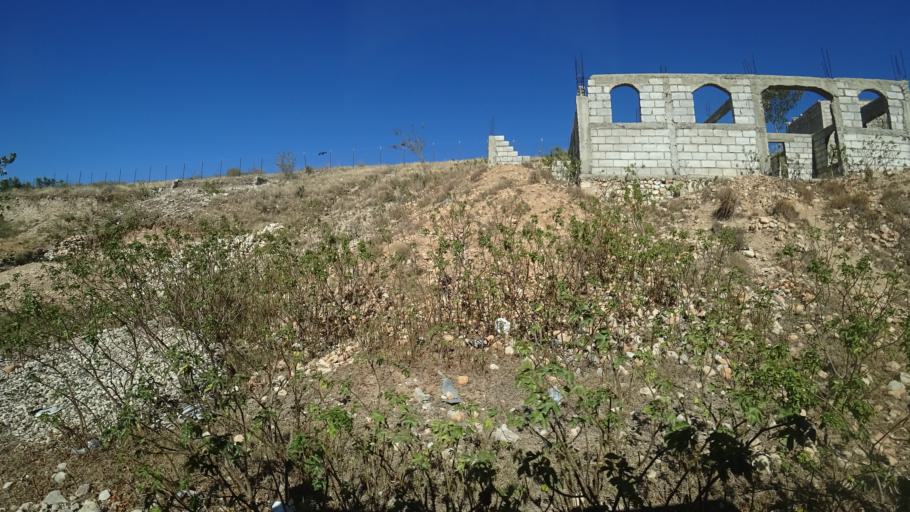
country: HT
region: Ouest
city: Cabaret
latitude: 18.6911
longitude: -72.3203
